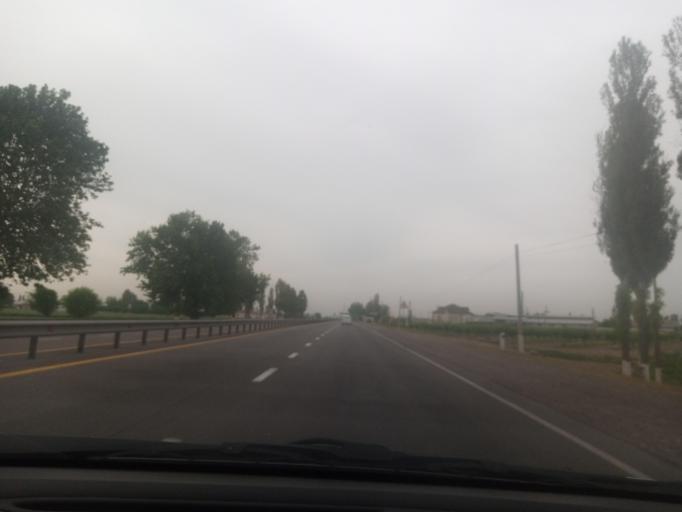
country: UZ
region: Toshkent Shahri
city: Bektemir
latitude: 41.1392
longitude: 69.4335
